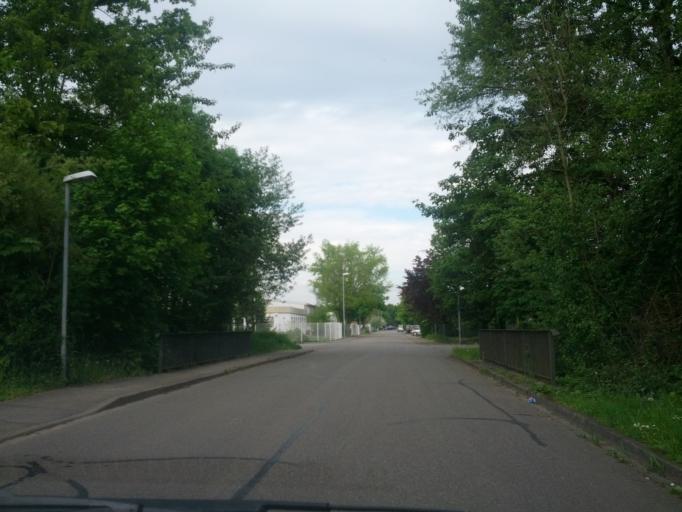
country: DE
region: Baden-Wuerttemberg
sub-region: Freiburg Region
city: Teningen
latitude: 48.1049
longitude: 7.7822
